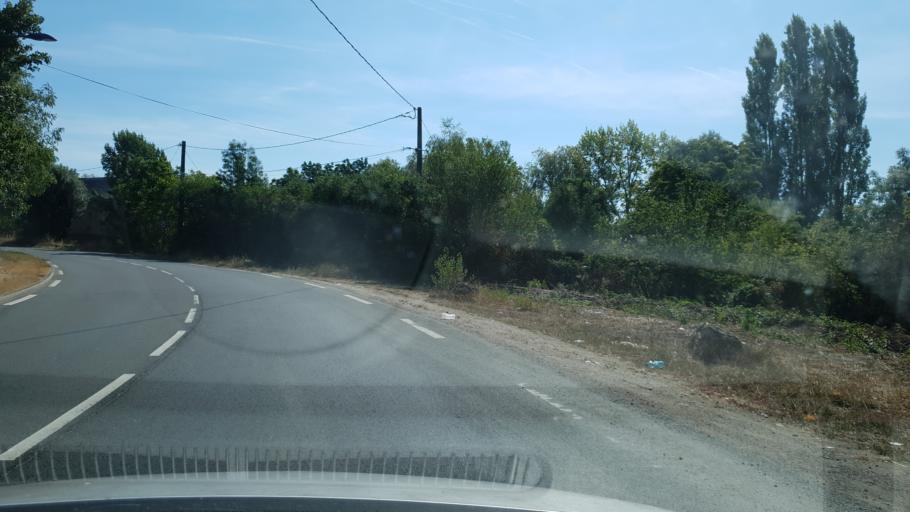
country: FR
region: Centre
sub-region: Departement d'Indre-et-Loire
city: La Riche
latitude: 47.3747
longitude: 0.6460
